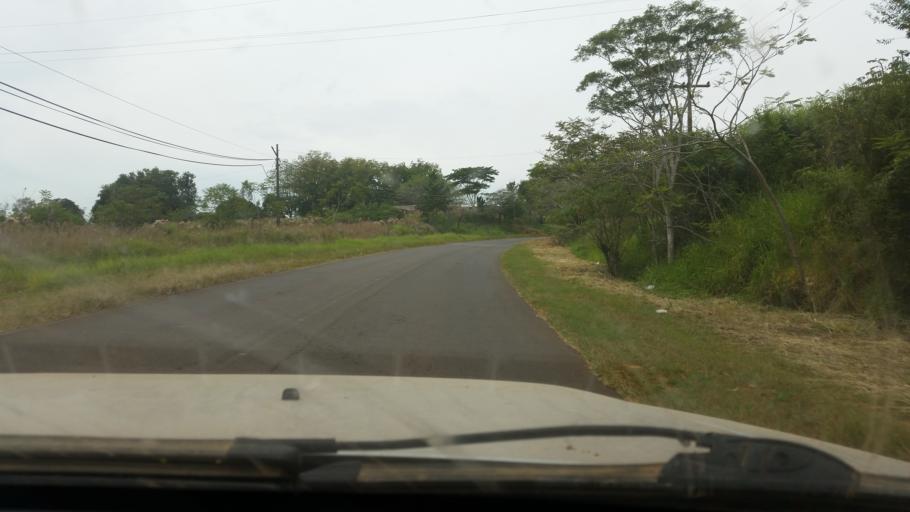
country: PY
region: Guaira
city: Independencia
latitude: -25.7020
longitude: -56.1977
